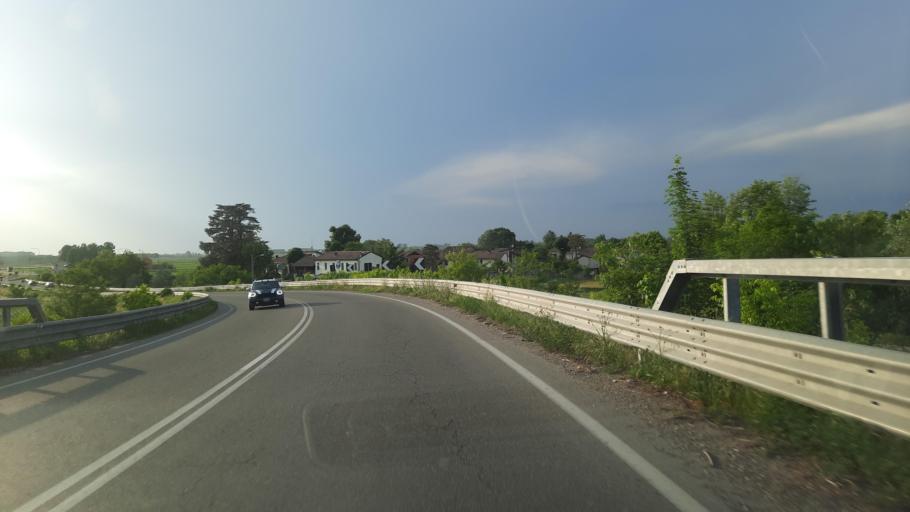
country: IT
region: Lombardy
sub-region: Provincia di Pavia
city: Cergnago
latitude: 45.2380
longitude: 8.7883
